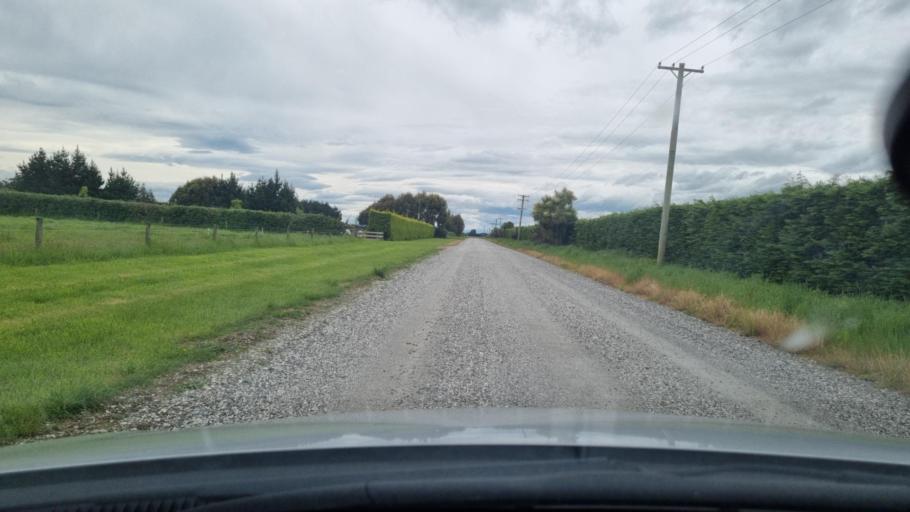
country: NZ
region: Southland
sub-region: Invercargill City
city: Invercargill
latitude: -46.3746
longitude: 168.2990
